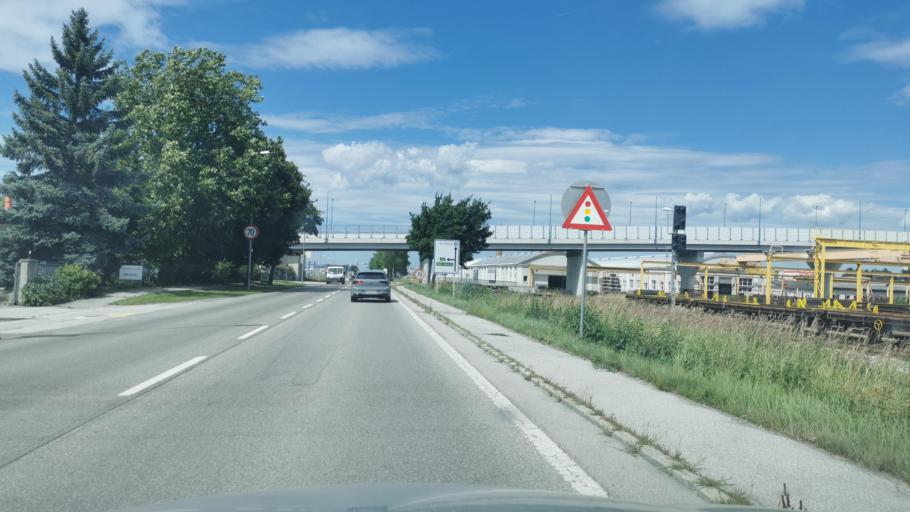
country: AT
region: Lower Austria
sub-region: Politischer Bezirk Sankt Polten
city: Wilhelmsburg
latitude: 48.1514
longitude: 15.6144
